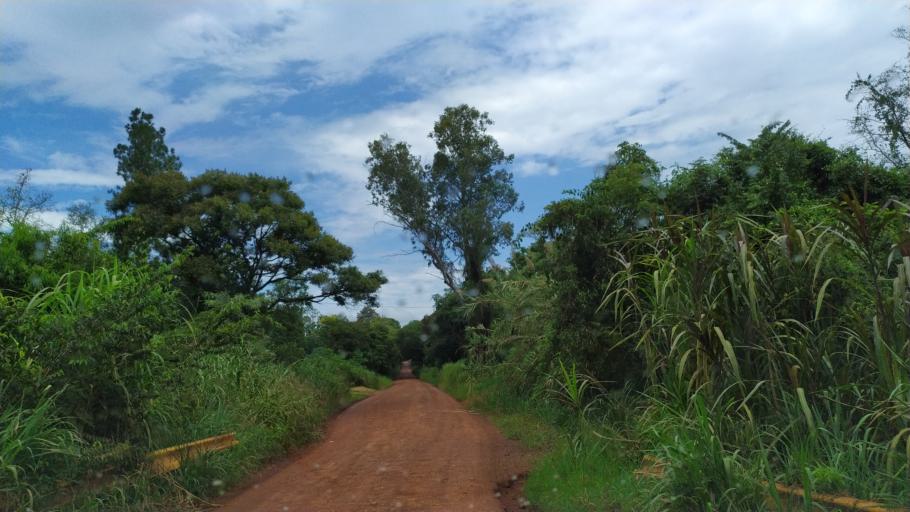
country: AR
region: Misiones
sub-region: Departamento de Eldorado
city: Eldorado
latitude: -26.4306
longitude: -54.6046
